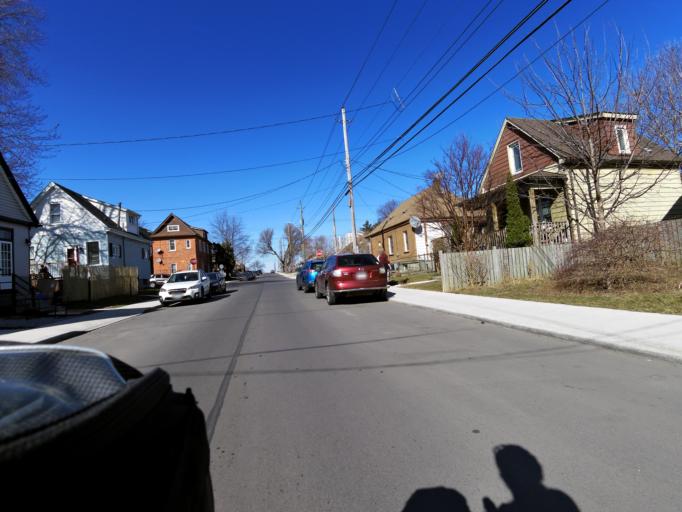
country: CA
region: Ontario
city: Hamilton
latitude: 43.2696
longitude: -79.8551
